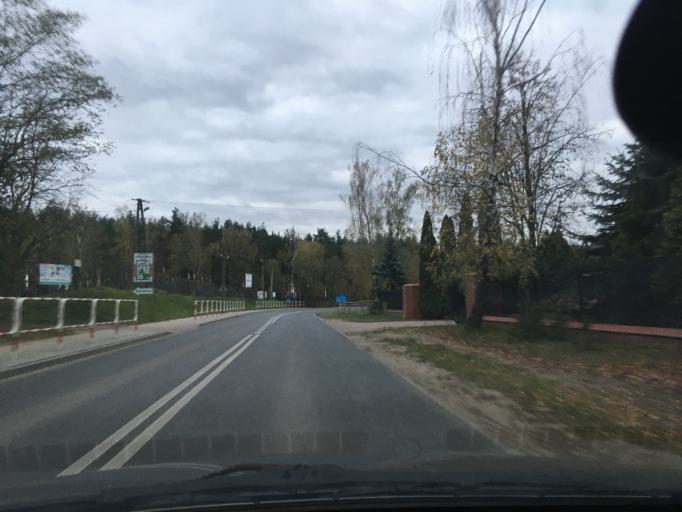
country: PL
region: Masovian Voivodeship
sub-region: Powiat piaseczynski
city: Lesznowola
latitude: 52.0678
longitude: 20.9340
